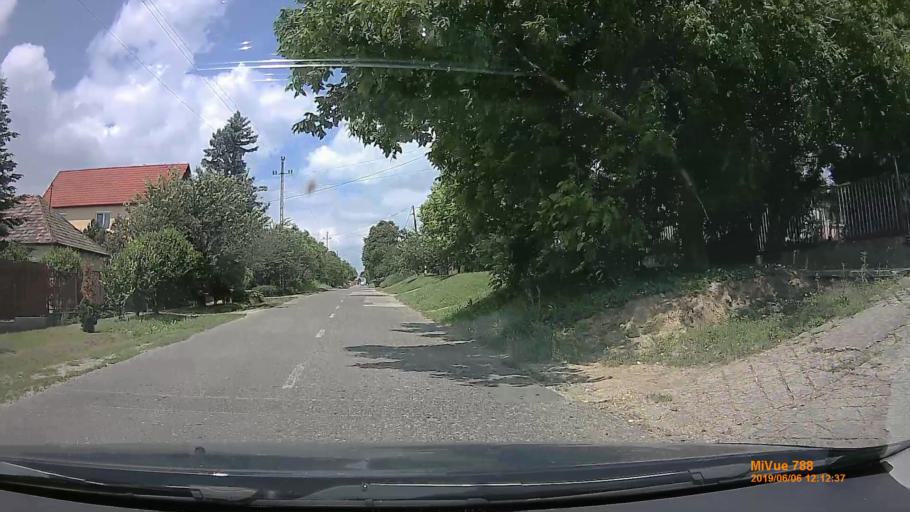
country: HU
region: Pest
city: Kerepes
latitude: 47.5761
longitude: 19.2647
